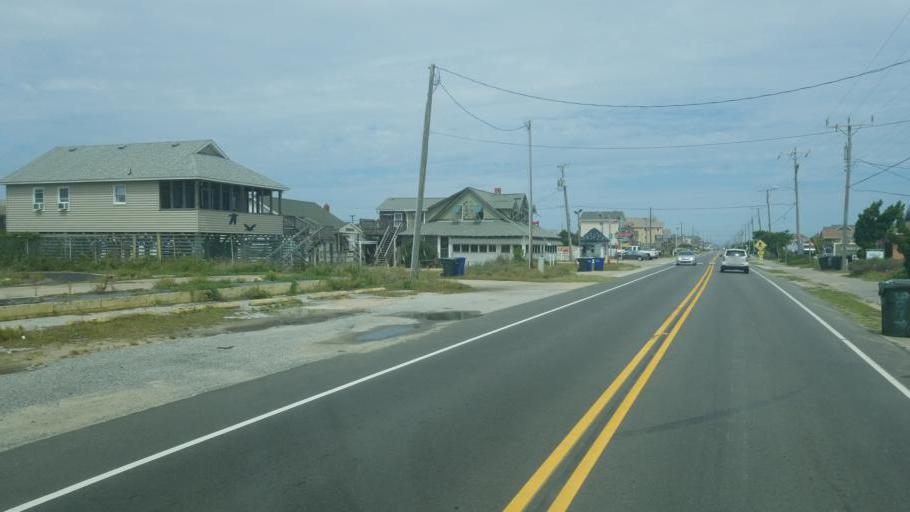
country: US
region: North Carolina
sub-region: Dare County
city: Nags Head
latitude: 35.9785
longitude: -75.6361
